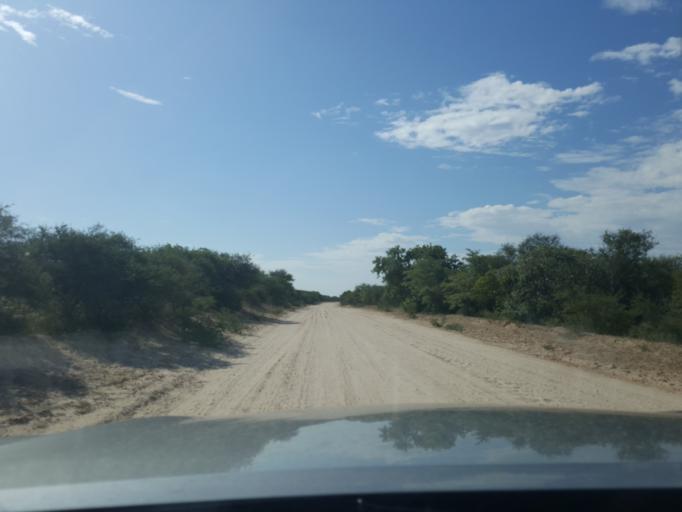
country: BW
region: Kweneng
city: Khudumelapye
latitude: -23.4851
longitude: 24.6945
